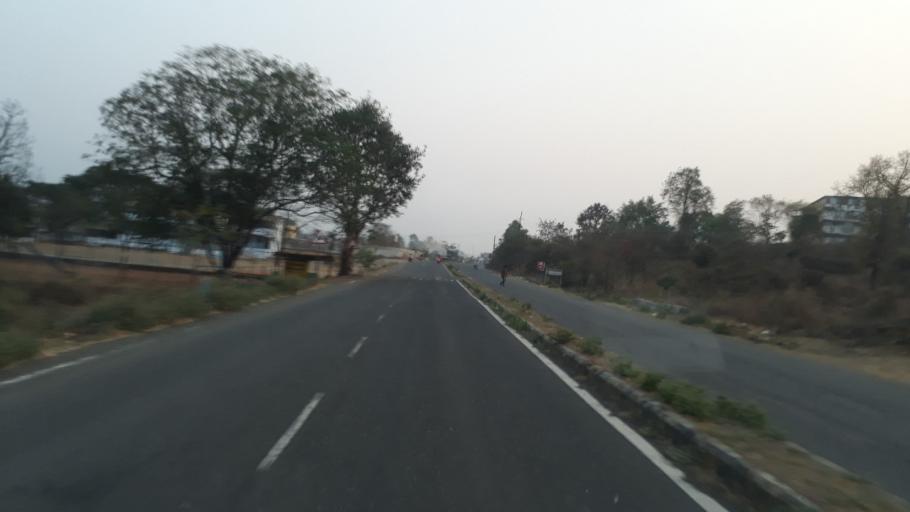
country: IN
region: Maharashtra
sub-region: Raigarh
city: Neral
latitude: 18.9735
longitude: 73.3292
